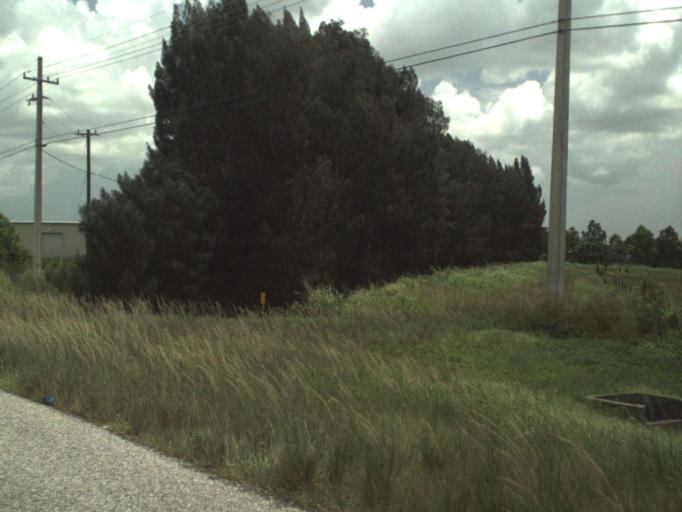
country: US
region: Florida
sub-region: Saint Lucie County
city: Fort Pierce South
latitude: 27.3889
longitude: -80.4622
